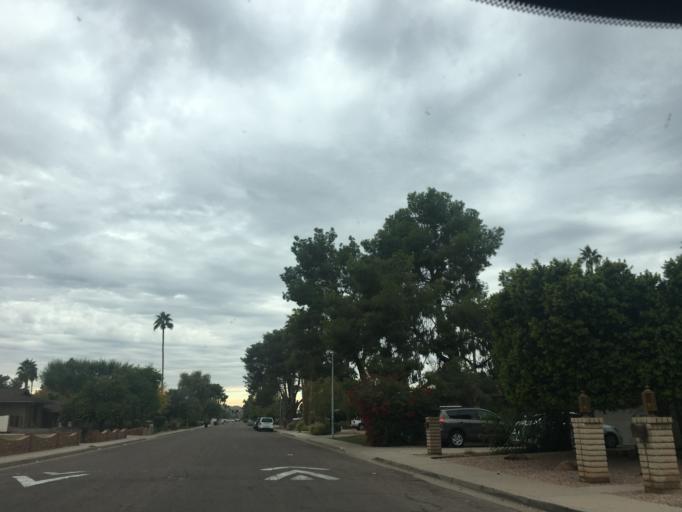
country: US
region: Arizona
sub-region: Maricopa County
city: Guadalupe
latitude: 33.3674
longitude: -111.9246
